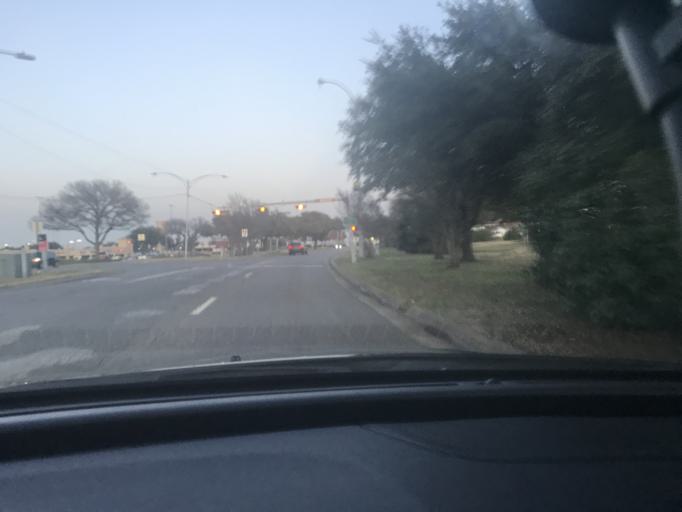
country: US
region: Texas
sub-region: Tarrant County
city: Arlington
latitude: 32.7652
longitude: -97.0998
